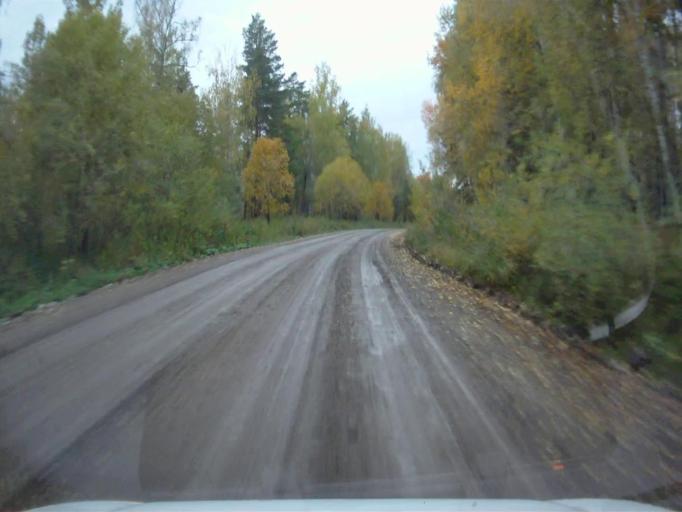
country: RU
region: Chelyabinsk
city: Nyazepetrovsk
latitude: 56.1117
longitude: 59.3707
